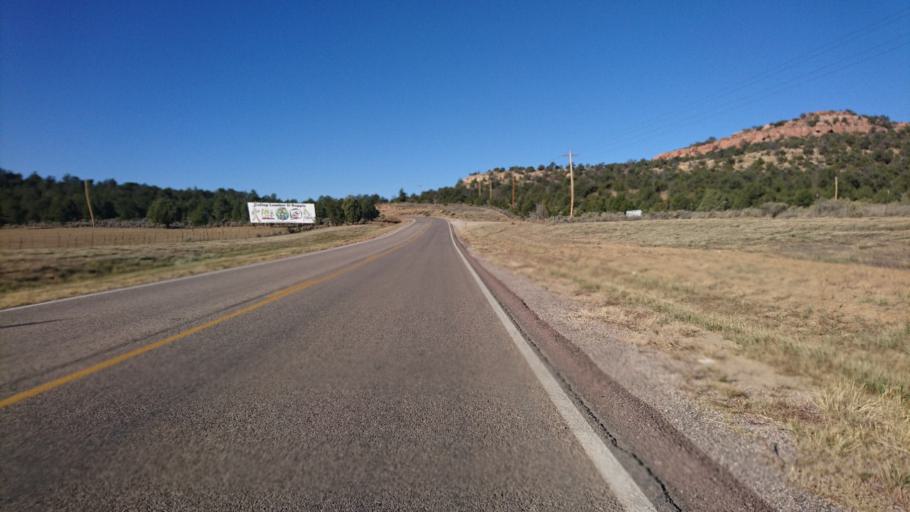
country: US
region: New Mexico
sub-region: McKinley County
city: Black Rock
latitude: 35.1320
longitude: -108.5213
